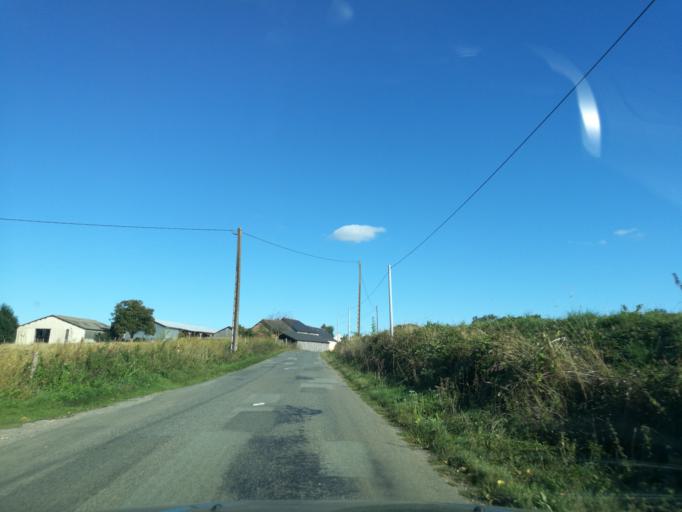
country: FR
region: Brittany
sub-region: Departement d'Ille-et-Vilaine
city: Montauban-de-Bretagne
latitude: 48.1702
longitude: -2.0081
